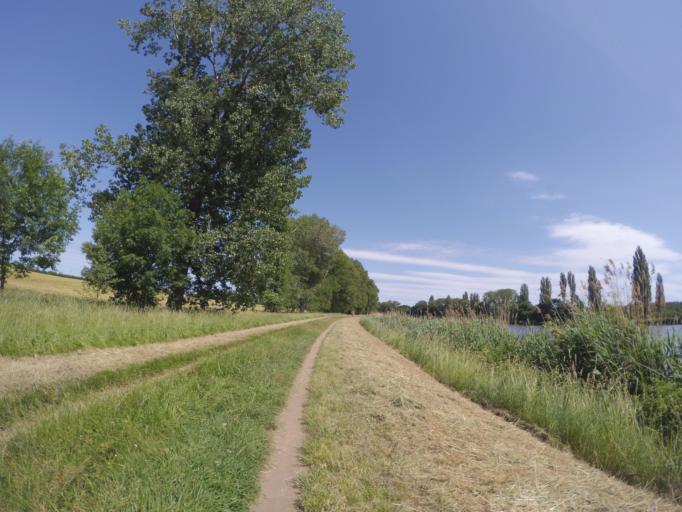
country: CZ
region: Central Bohemia
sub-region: Okres Nymburk
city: Sadska
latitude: 50.1704
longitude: 14.9911
